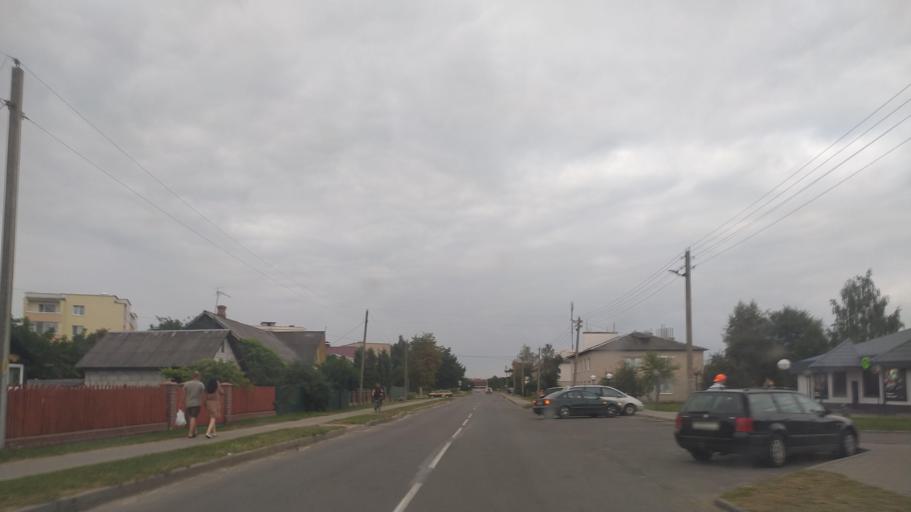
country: BY
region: Brest
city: Byaroza
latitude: 52.5274
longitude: 24.9831
